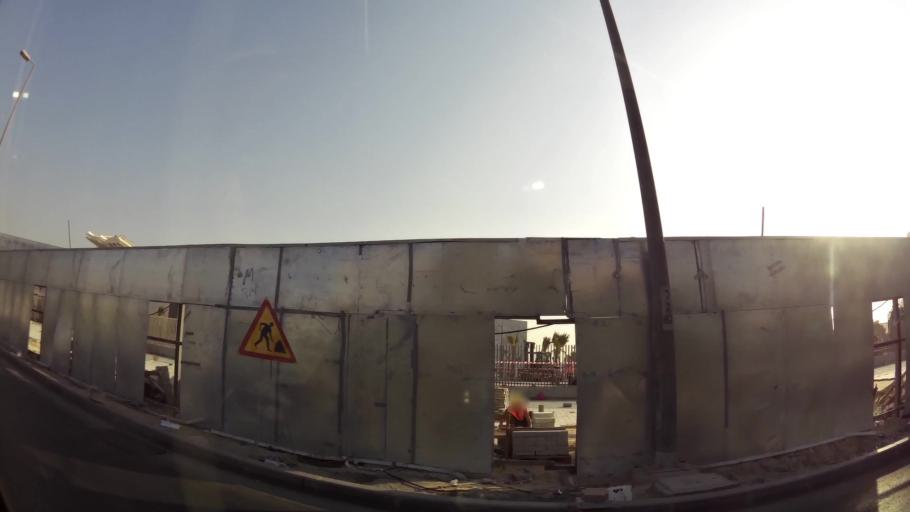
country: KW
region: Muhafazat Hawalli
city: Hawalli
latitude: 29.3420
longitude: 48.0402
